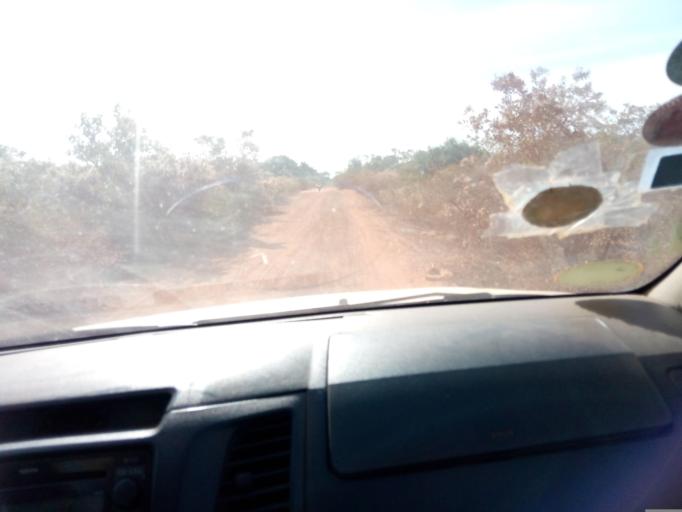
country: ML
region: Sikasso
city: Sikasso
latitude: 11.8794
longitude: -6.0378
